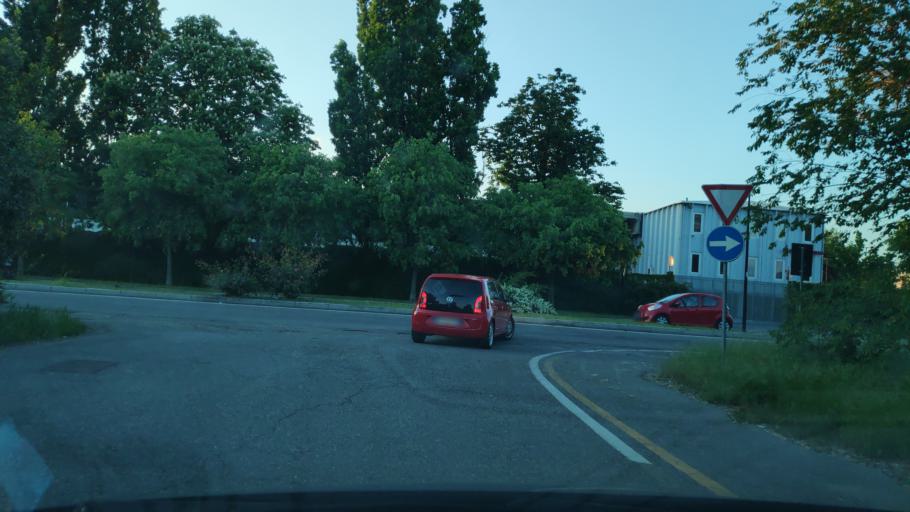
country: IT
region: Lombardy
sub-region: Citta metropolitana di Milano
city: Segrate
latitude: 45.4834
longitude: 9.2988
